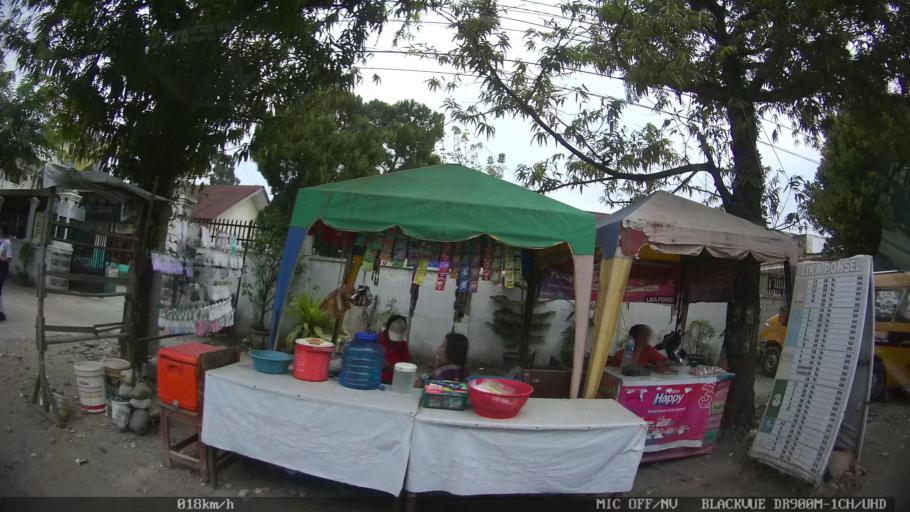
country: ID
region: North Sumatra
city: Medan
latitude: 3.5627
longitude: 98.7028
